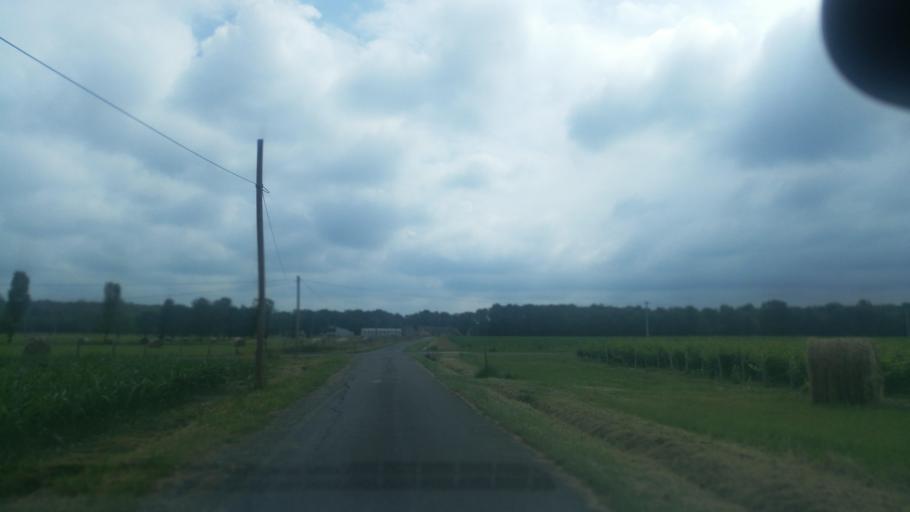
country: FR
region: Centre
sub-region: Departement du Loir-et-Cher
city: Saint-Romain-sur-Cher
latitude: 47.3455
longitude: 1.4451
